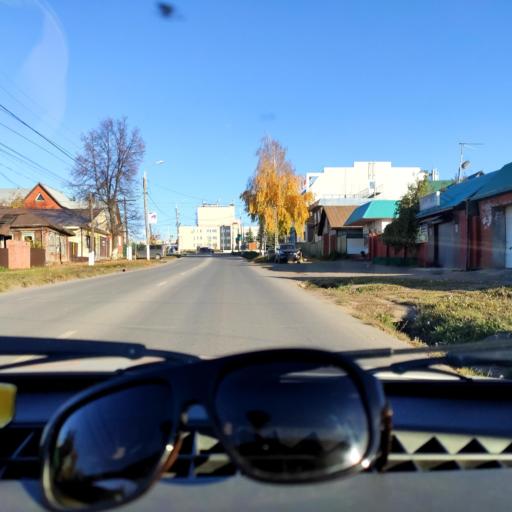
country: RU
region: Bashkortostan
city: Blagoveshchensk
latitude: 55.0445
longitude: 55.9597
